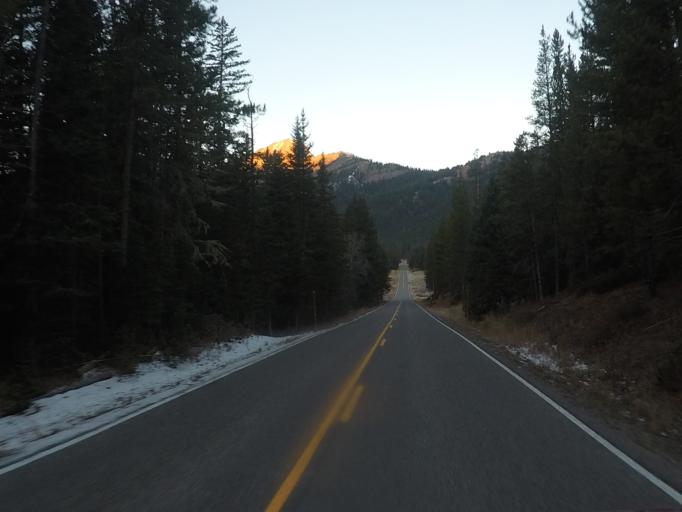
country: US
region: Montana
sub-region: Stillwater County
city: Absarokee
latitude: 45.0041
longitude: -110.0286
